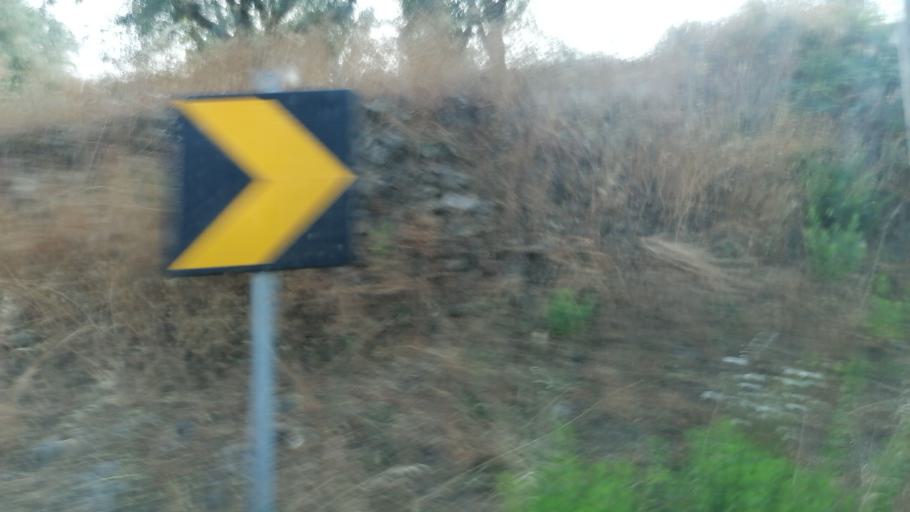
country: PT
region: Viseu
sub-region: Sao Joao da Pesqueira
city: Sao Joao da Pesqueira
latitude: 41.1418
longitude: -7.3999
